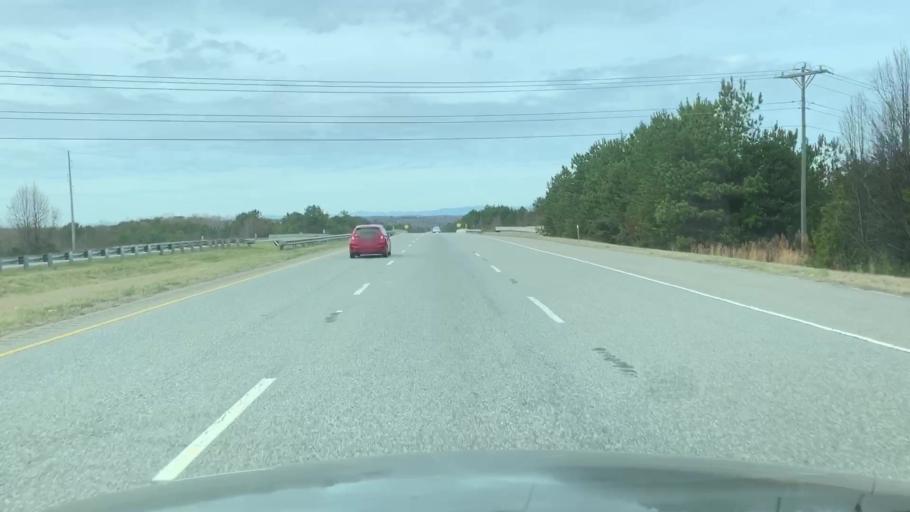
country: US
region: South Carolina
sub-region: Greenville County
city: Golden Grove
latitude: 34.7424
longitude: -82.4367
